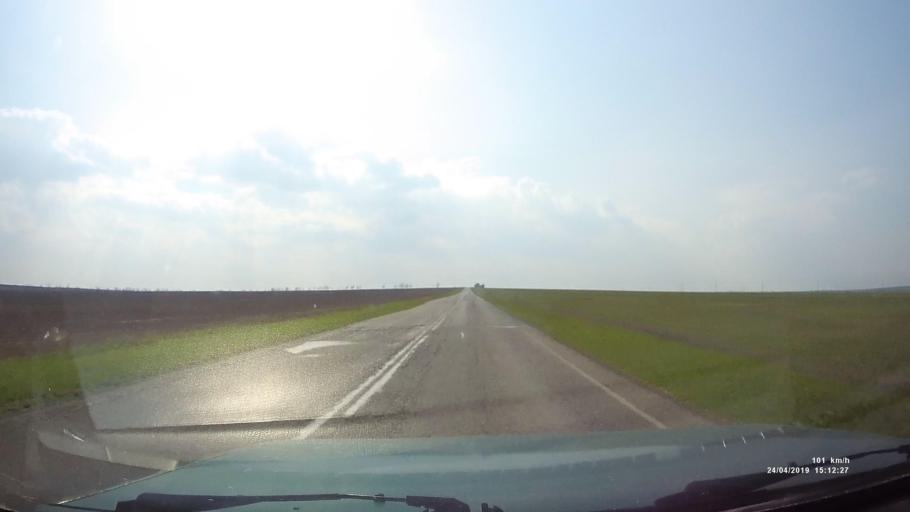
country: RU
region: Rostov
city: Remontnoye
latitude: 46.5464
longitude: 43.3003
